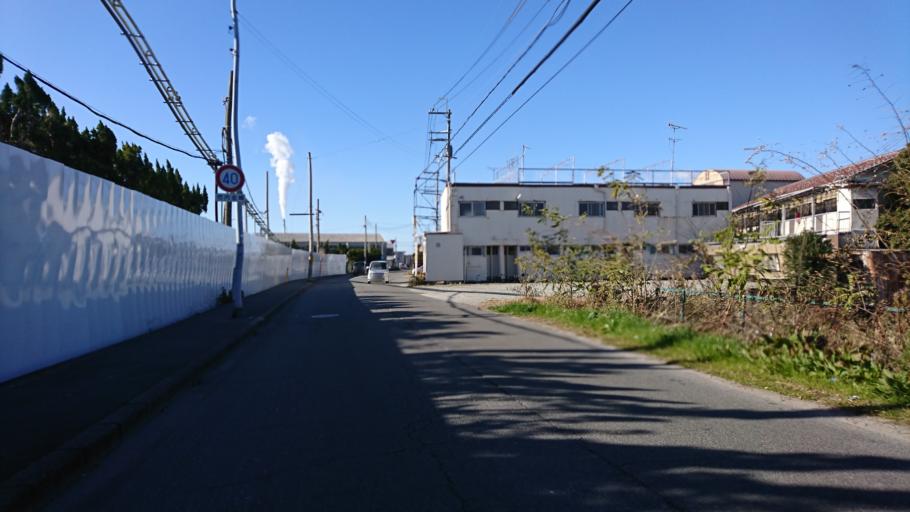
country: JP
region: Hyogo
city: Kakogawacho-honmachi
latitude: 34.7667
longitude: 134.7843
